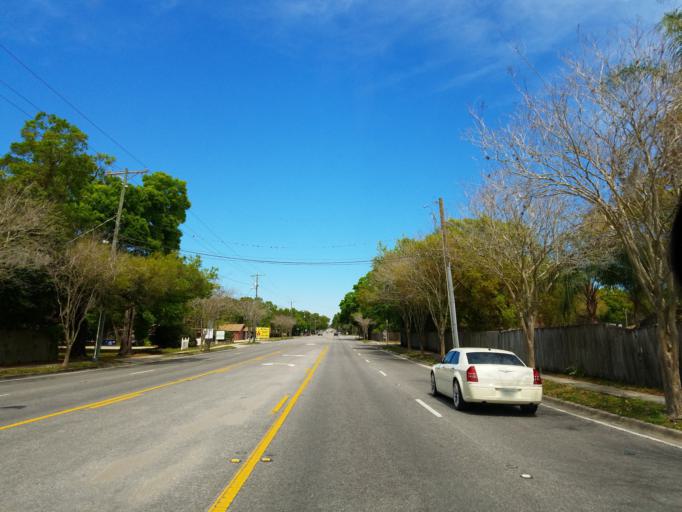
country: US
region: Florida
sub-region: Hillsborough County
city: Seffner
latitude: 27.9631
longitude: -82.2858
